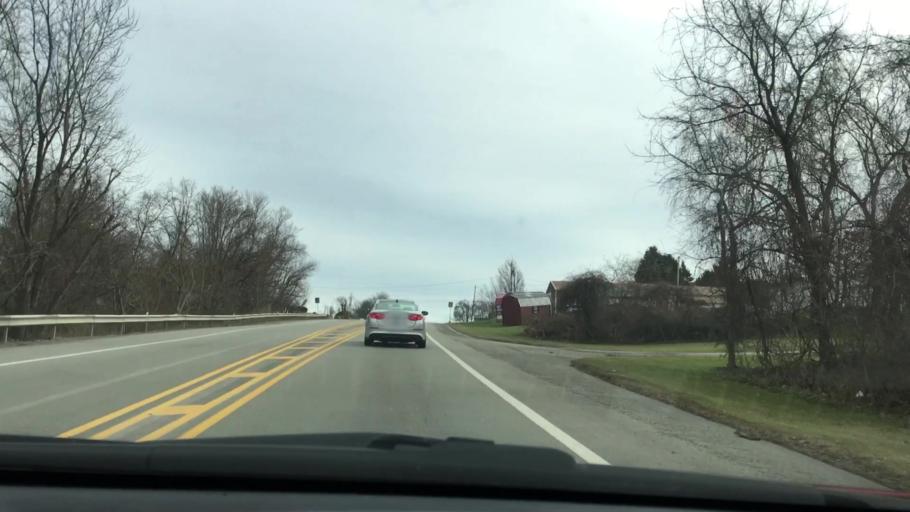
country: US
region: Pennsylvania
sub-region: Fayette County
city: Masontown
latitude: 39.8922
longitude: -79.8464
